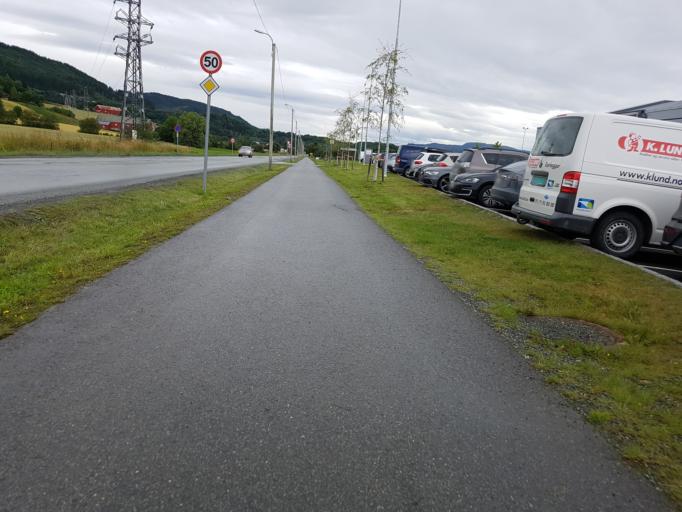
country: NO
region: Sor-Trondelag
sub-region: Trondheim
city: Trondheim
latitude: 63.3876
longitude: 10.4345
